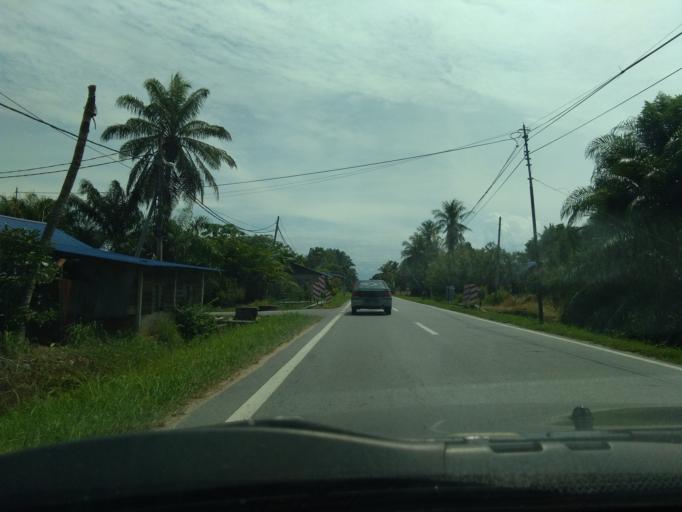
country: MY
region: Perak
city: Bagan Serai
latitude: 5.0375
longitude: 100.5695
